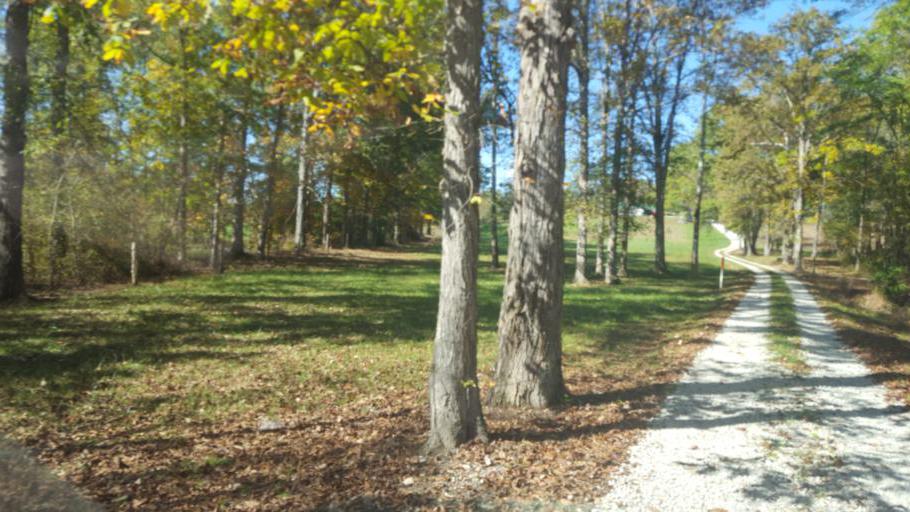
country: US
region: Kentucky
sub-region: Fleming County
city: Flemingsburg
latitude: 38.4622
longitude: -83.5713
